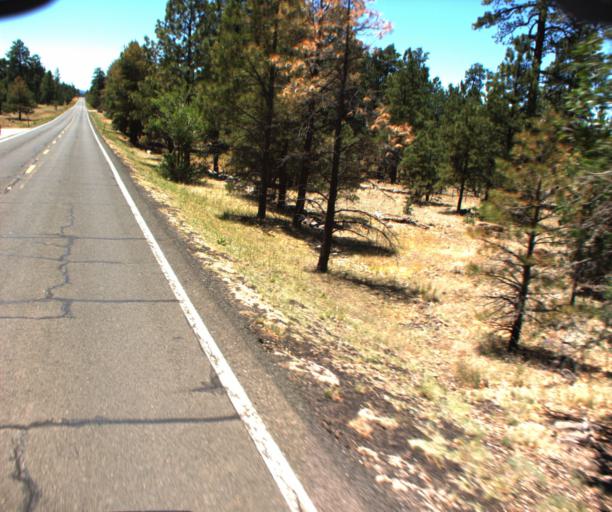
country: US
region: Arizona
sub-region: Gila County
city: Pine
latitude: 34.5772
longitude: -111.2652
